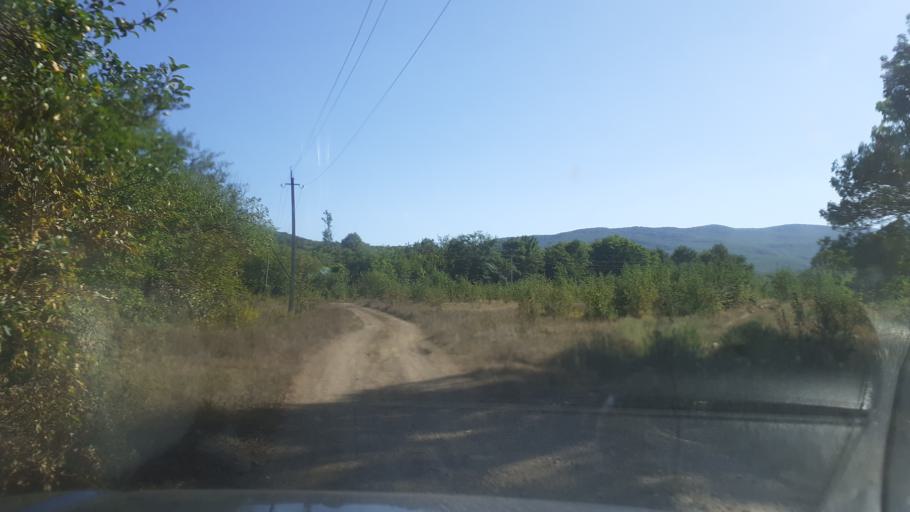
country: RU
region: Krasnodarskiy
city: Azovskaya
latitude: 44.7222
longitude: 38.5338
